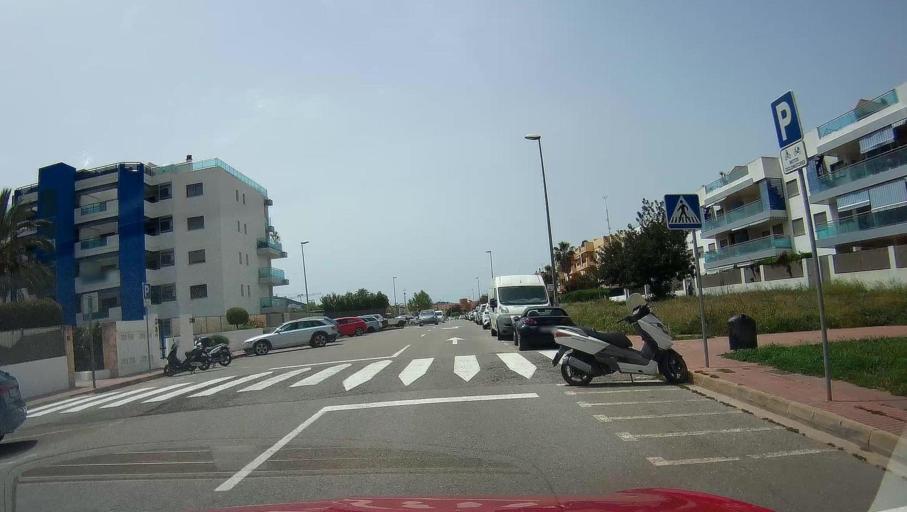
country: ES
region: Balearic Islands
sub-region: Illes Balears
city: Santa Eularia des Riu
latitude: 38.9907
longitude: 1.5463
